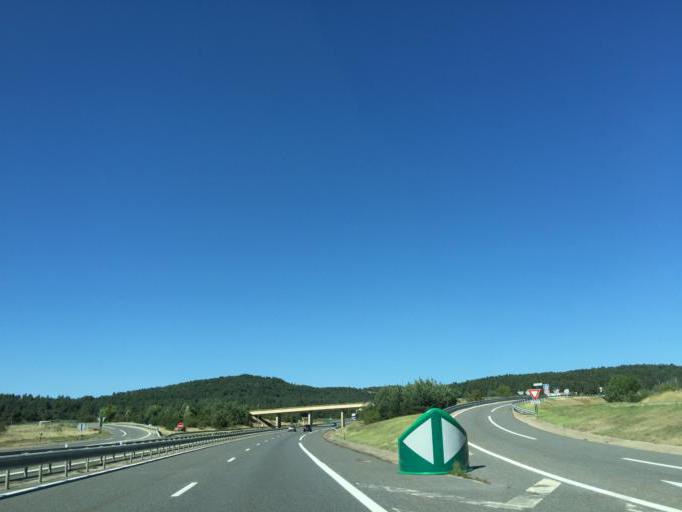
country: FR
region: Midi-Pyrenees
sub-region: Departement de l'Aveyron
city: Severac-le-Chateau
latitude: 44.3822
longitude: 3.1169
